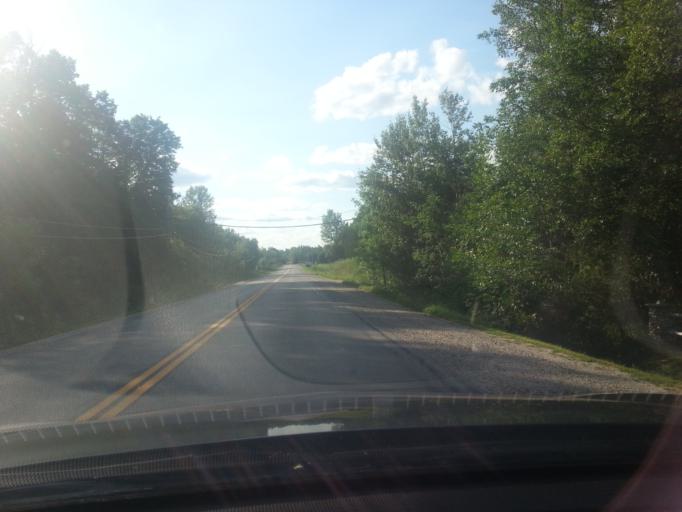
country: CA
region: Ontario
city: Carleton Place
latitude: 45.0866
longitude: -76.2462
